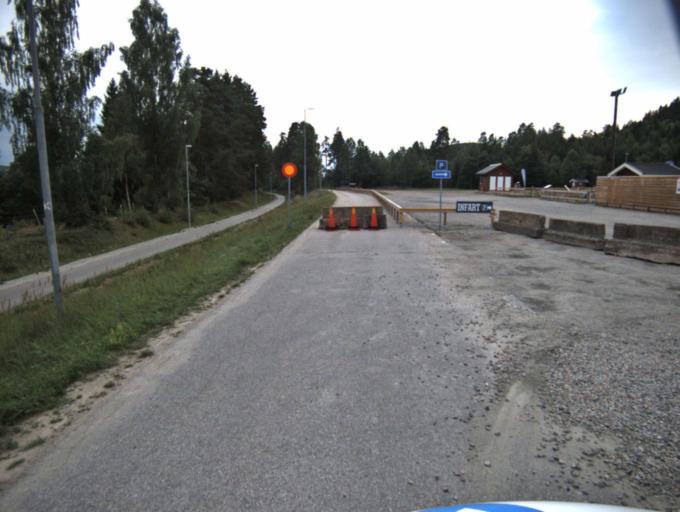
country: SE
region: Vaestra Goetaland
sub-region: Ulricehamns Kommun
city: Ulricehamn
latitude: 57.8196
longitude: 13.4127
